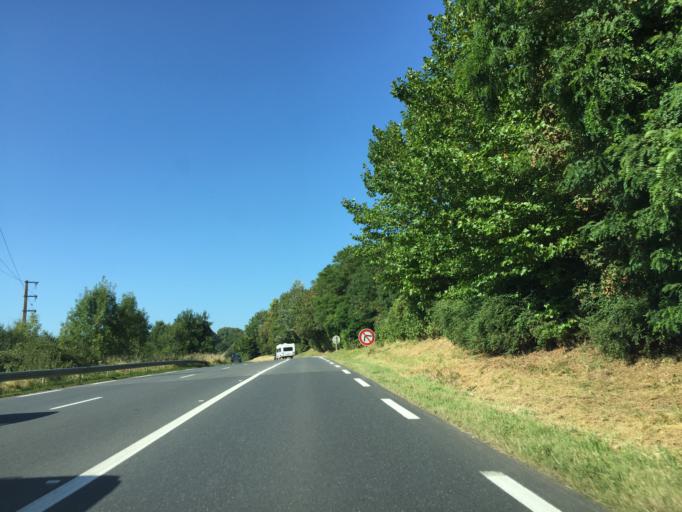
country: FR
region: Lower Normandy
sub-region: Departement du Calvados
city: Saint-Gatien-des-Bois
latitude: 49.2675
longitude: 0.2176
